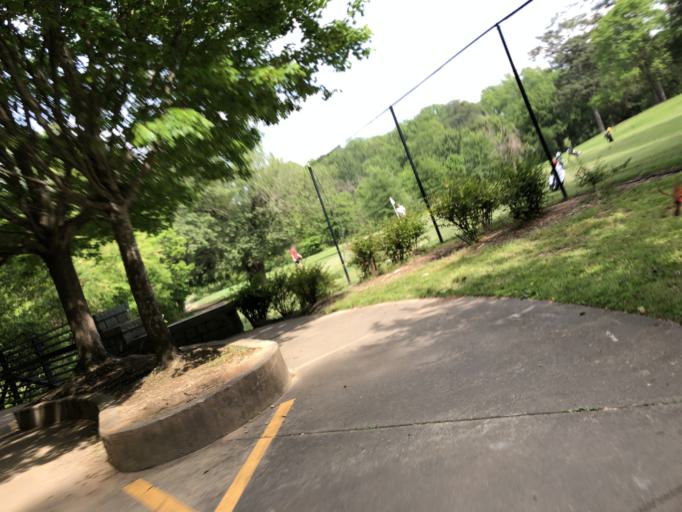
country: US
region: Georgia
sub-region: DeKalb County
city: Druid Hills
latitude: 33.7714
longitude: -84.3384
